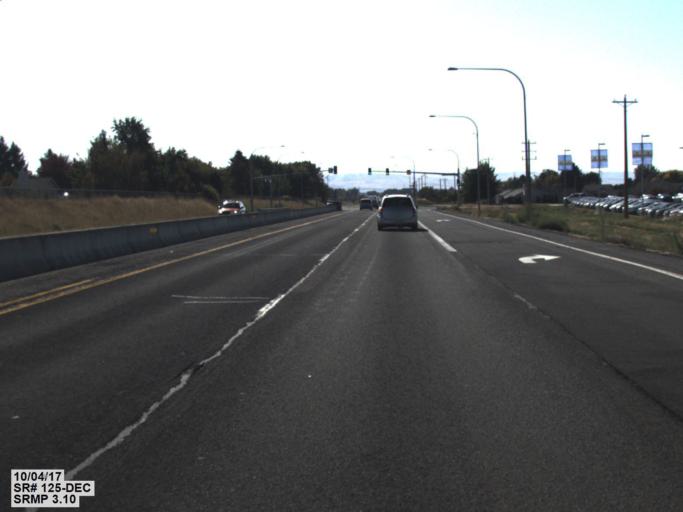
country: US
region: Washington
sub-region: Walla Walla County
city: College Place
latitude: 46.0387
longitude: -118.3681
